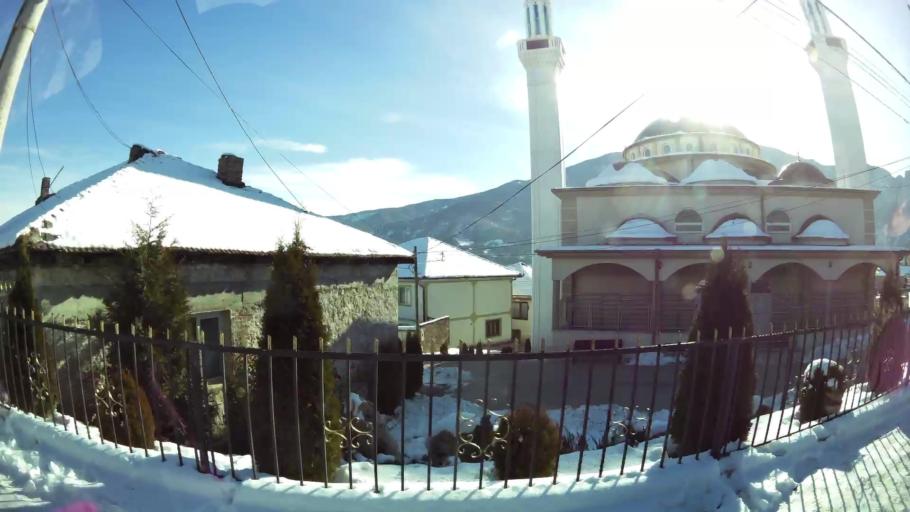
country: MK
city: Ljubin
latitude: 41.9793
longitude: 21.3032
